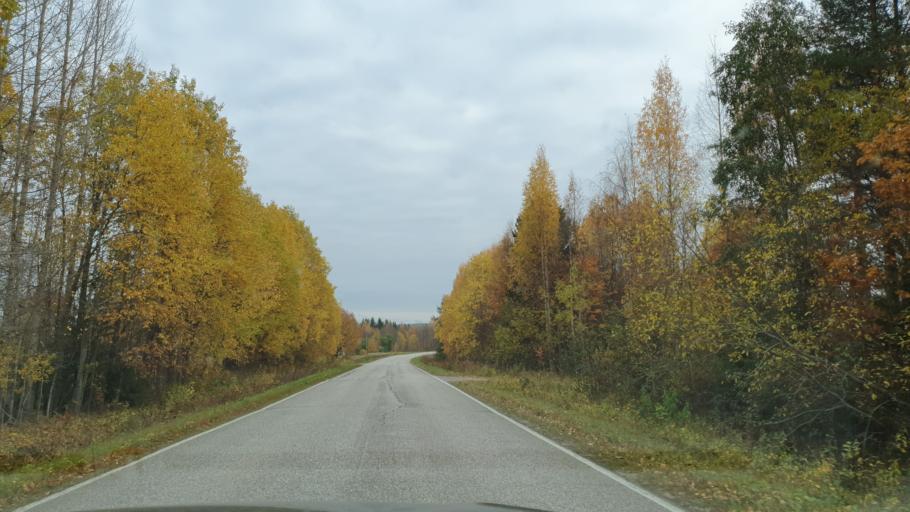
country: FI
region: Kainuu
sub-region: Kajaani
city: Ristijaervi
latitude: 64.4685
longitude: 28.3027
